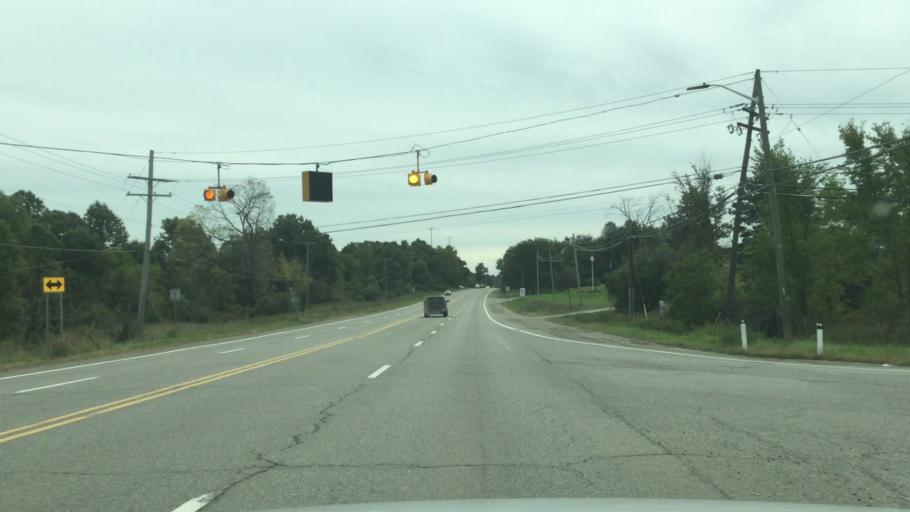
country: US
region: Michigan
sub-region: Oakland County
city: Ortonville
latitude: 42.7806
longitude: -83.4993
